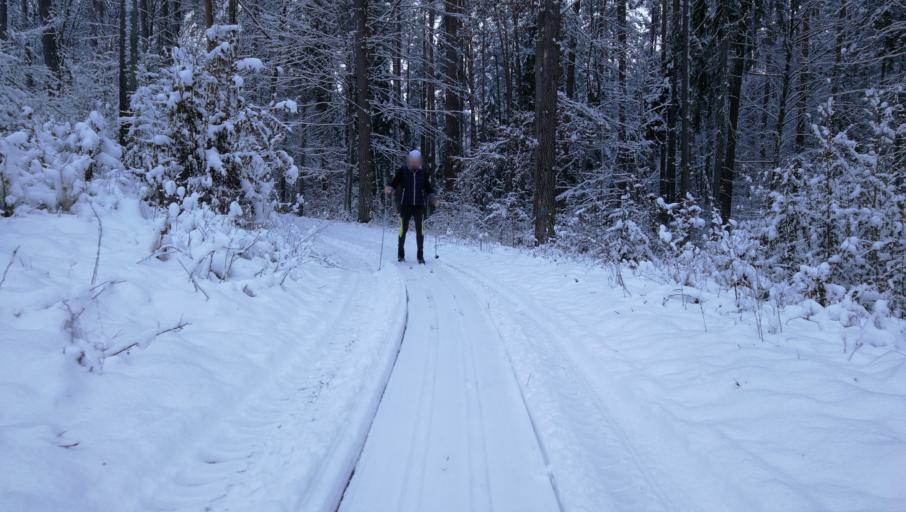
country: PL
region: Kujawsko-Pomorskie
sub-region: Powiat brodnicki
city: Gorzno
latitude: 53.2070
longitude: 19.6965
